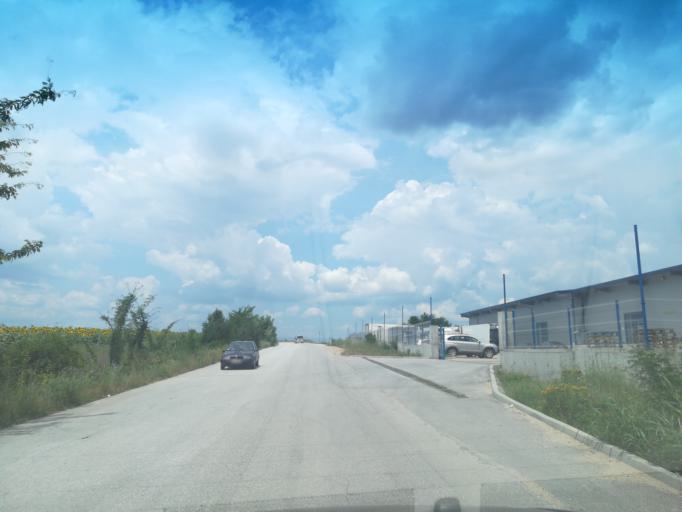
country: BG
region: Stara Zagora
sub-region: Obshtina Chirpan
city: Chirpan
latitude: 42.1798
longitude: 25.2069
